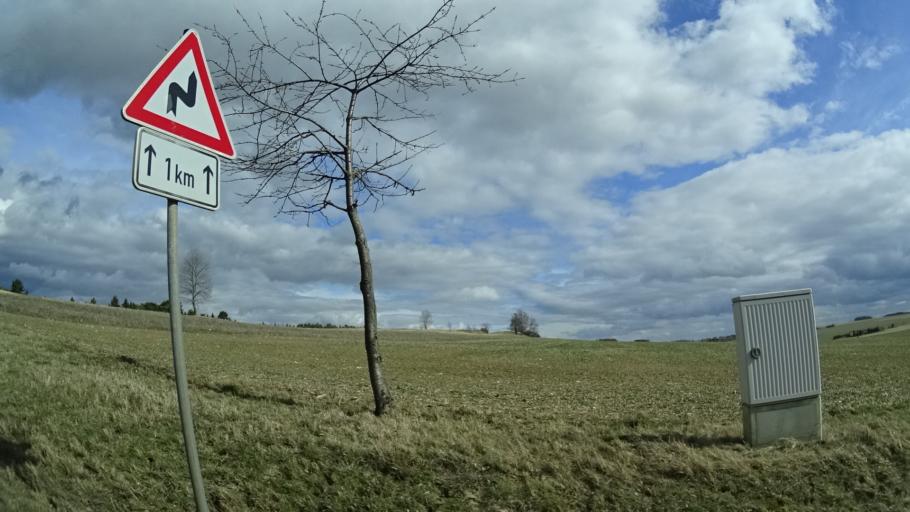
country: DE
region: Thuringia
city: Blankenhain
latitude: 50.8438
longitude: 11.3407
